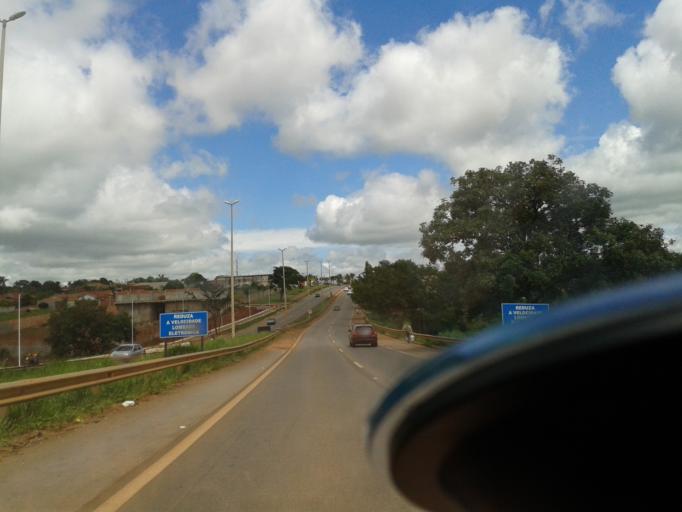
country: BR
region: Goias
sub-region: Goianira
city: Goianira
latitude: -16.5118
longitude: -49.4197
